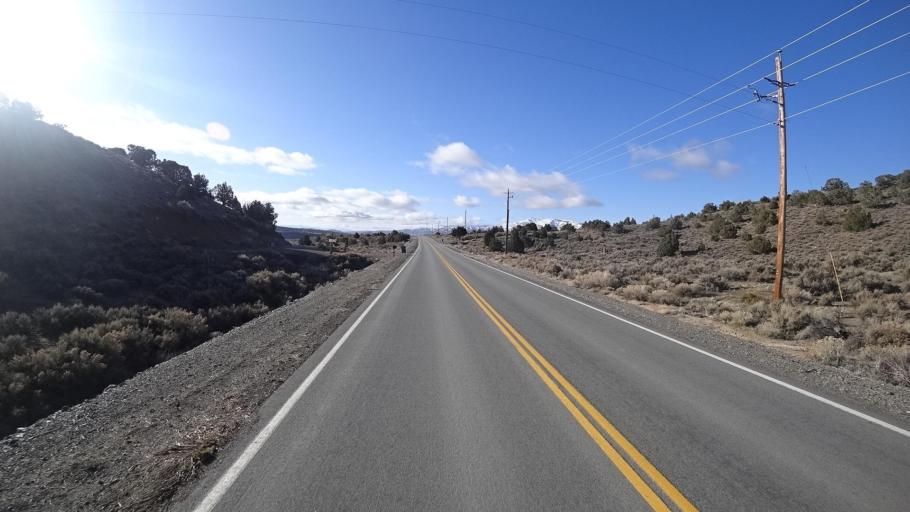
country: US
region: Nevada
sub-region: Washoe County
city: Lemmon Valley
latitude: 39.7294
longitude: -119.8812
